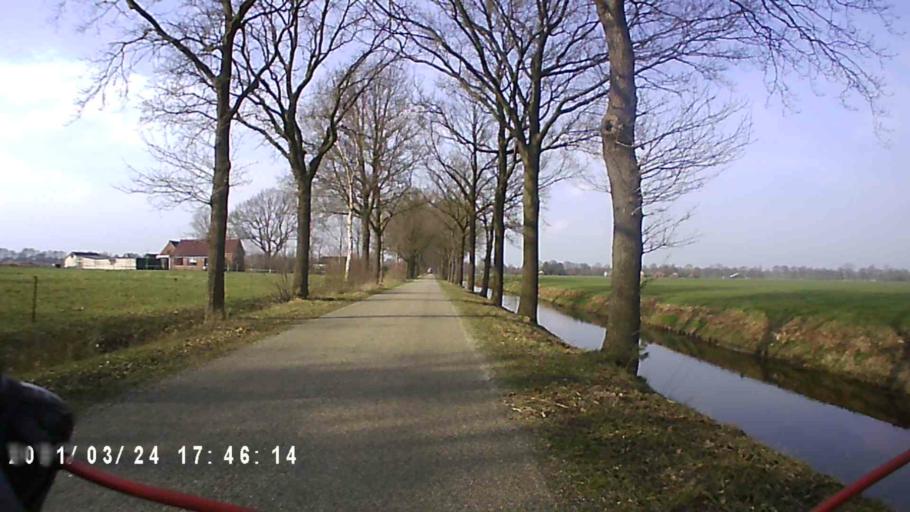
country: NL
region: Groningen
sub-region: Gemeente Leek
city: Leek
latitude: 53.1104
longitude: 6.3369
